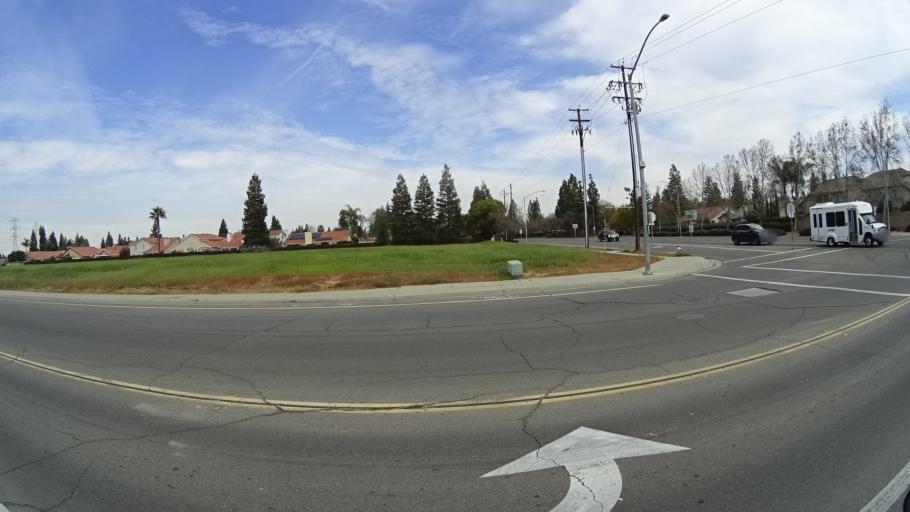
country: US
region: California
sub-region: Fresno County
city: West Park
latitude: 36.8298
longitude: -119.8899
